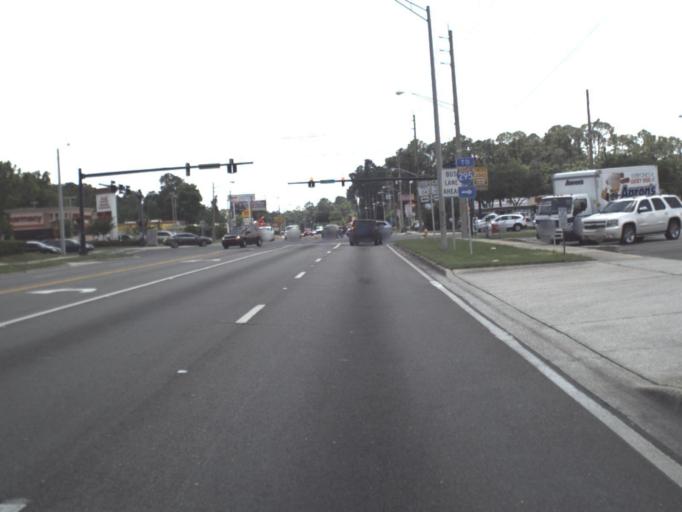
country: US
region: Florida
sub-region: Clay County
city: Bellair-Meadowbrook Terrace
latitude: 30.2493
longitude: -81.7431
